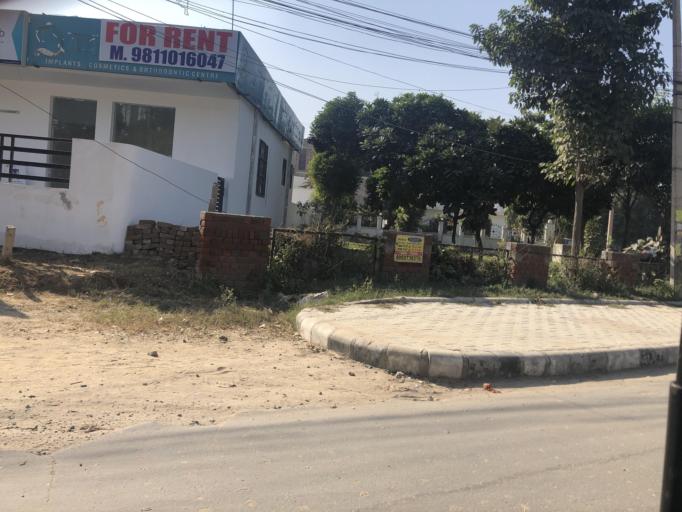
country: IN
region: Haryana
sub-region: Gurgaon
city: Gurgaon
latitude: 28.4521
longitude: 77.0668
